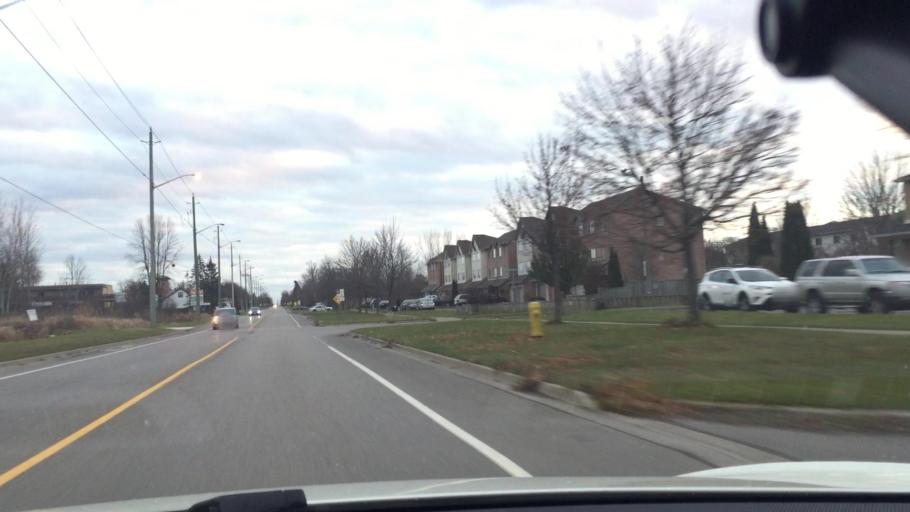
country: CA
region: Ontario
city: Oshawa
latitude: 43.9094
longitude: -78.7877
